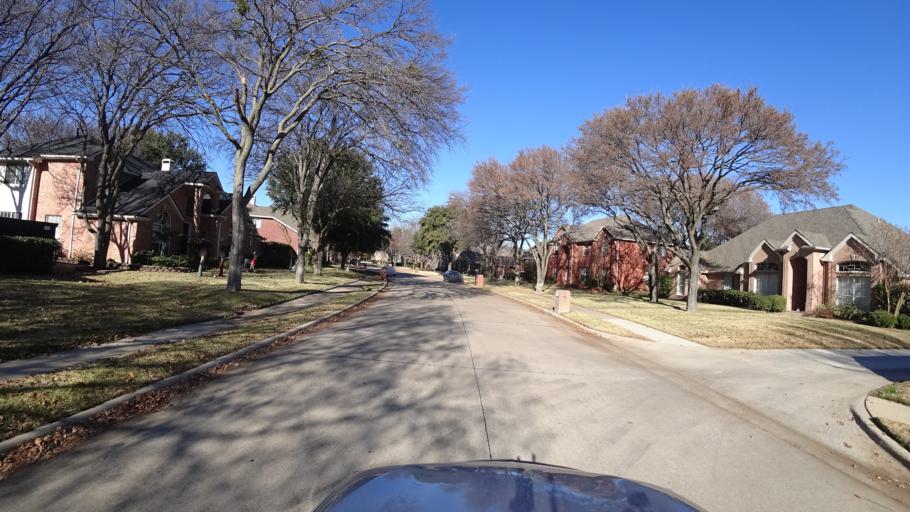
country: US
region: Texas
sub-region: Denton County
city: Lewisville
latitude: 33.0115
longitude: -97.0333
